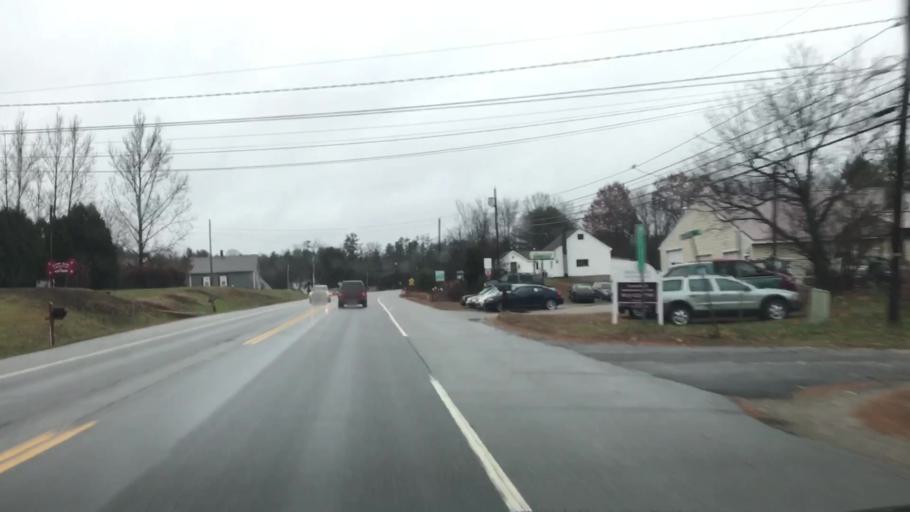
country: US
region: New Hampshire
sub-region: Merrimack County
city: Pittsfield
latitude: 43.2964
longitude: -71.3510
